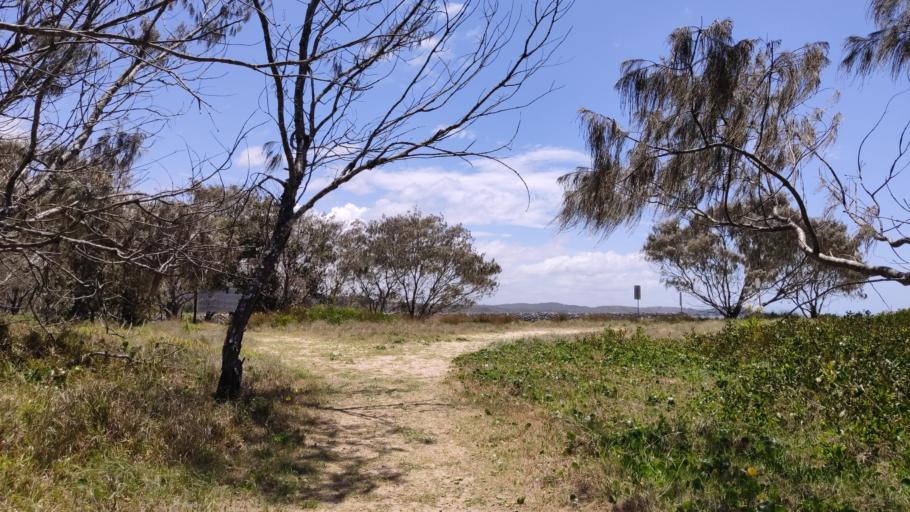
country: AU
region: New South Wales
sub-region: Port Macquarie-Hastings
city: North Haven
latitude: -31.6393
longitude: 152.8364
